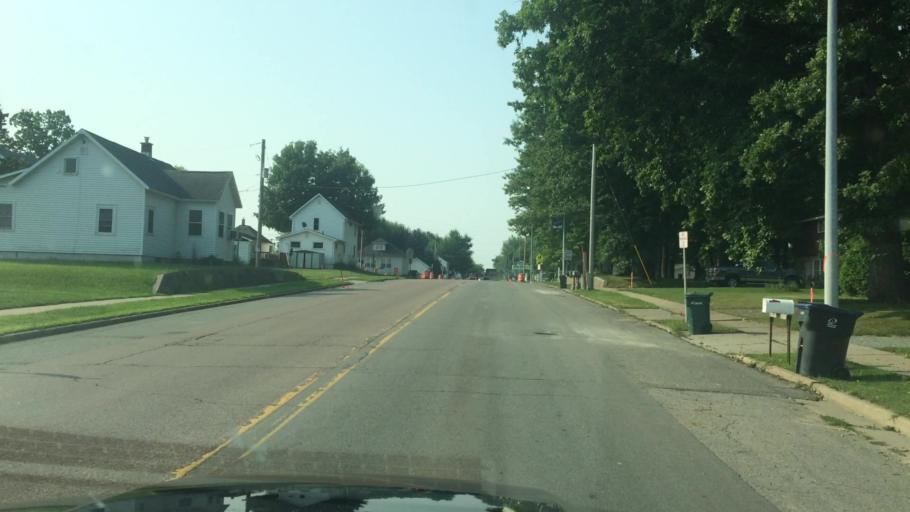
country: US
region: Wisconsin
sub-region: Marathon County
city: Stratford
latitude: 44.8062
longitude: -90.0792
